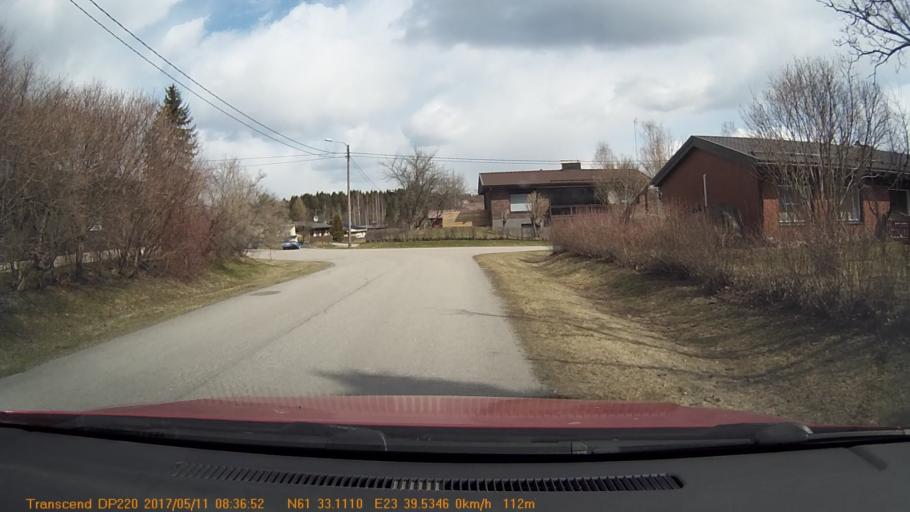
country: FI
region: Pirkanmaa
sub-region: Tampere
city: Yloejaervi
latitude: 61.5519
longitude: 23.6589
